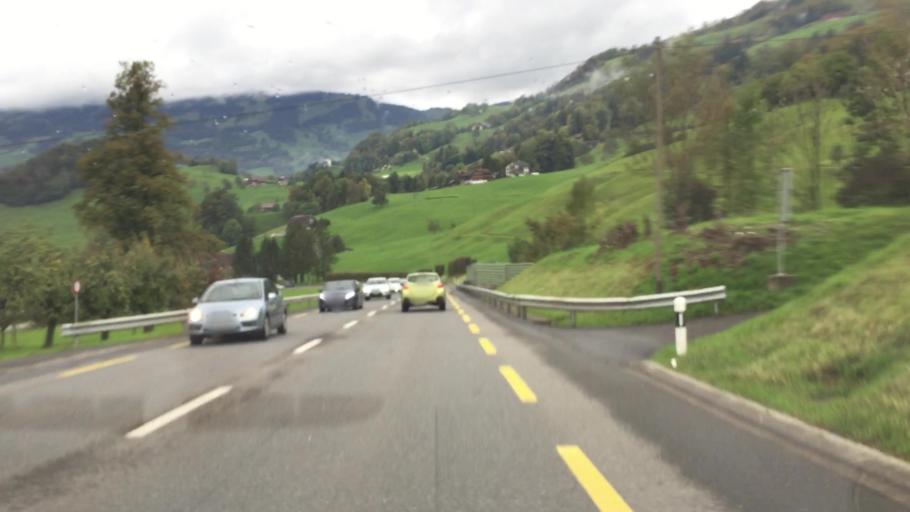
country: CH
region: Schwyz
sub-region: Bezirk Schwyz
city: Schwyz
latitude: 47.0328
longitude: 8.6413
